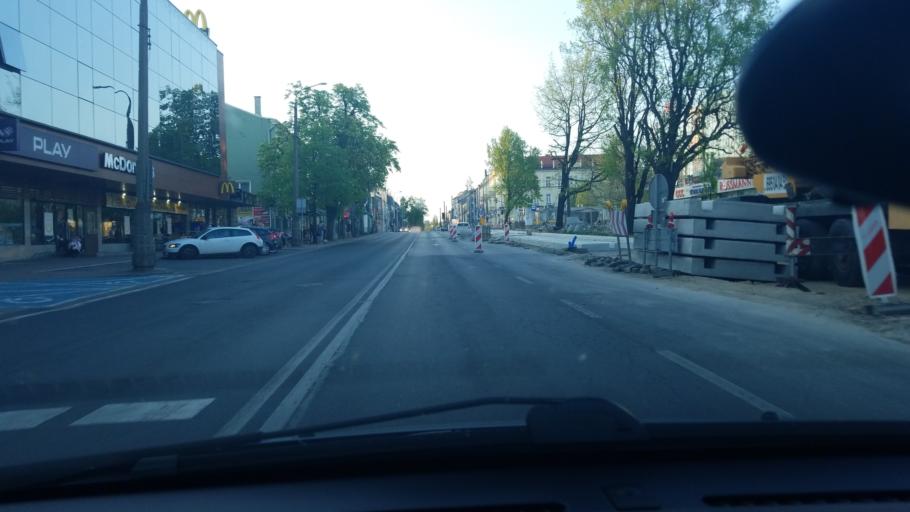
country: PL
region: Silesian Voivodeship
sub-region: Czestochowa
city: Czestochowa
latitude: 50.8106
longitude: 19.1181
